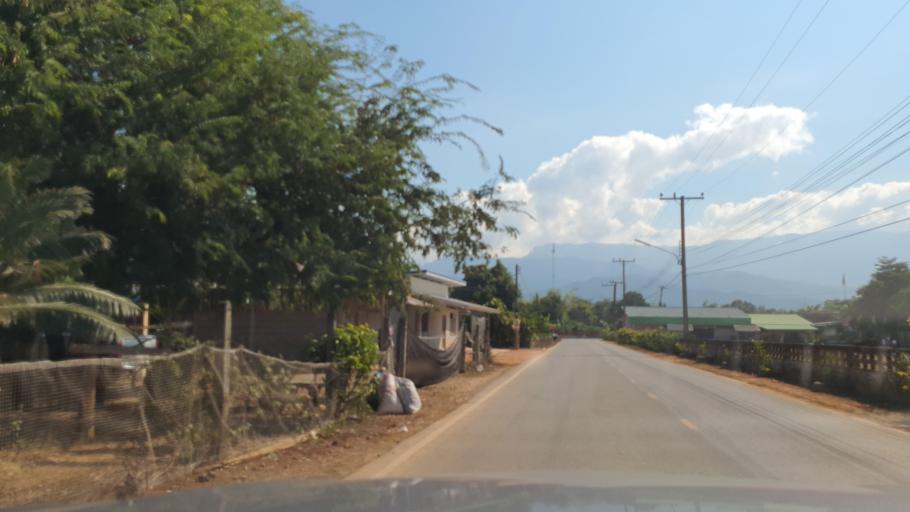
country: TH
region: Nan
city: Pua
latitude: 19.1442
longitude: 100.9233
